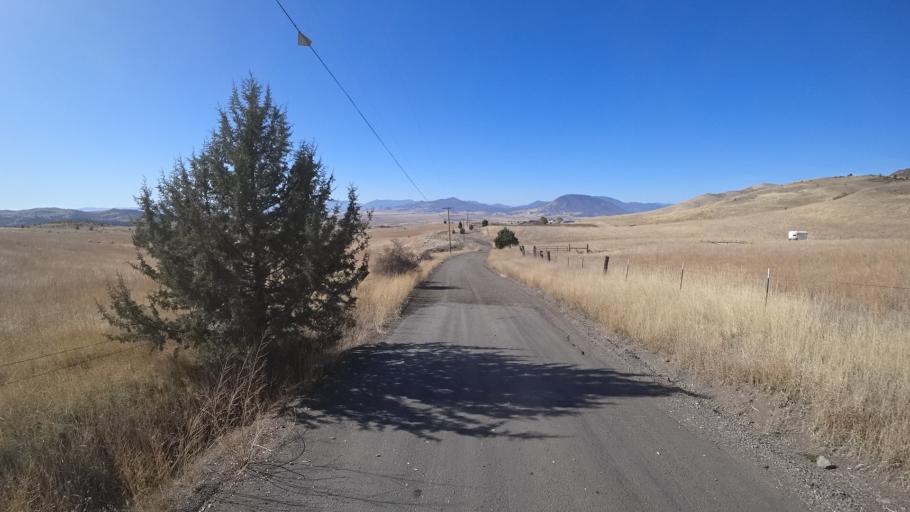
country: US
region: California
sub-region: Siskiyou County
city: Montague
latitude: 41.8302
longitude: -122.3541
